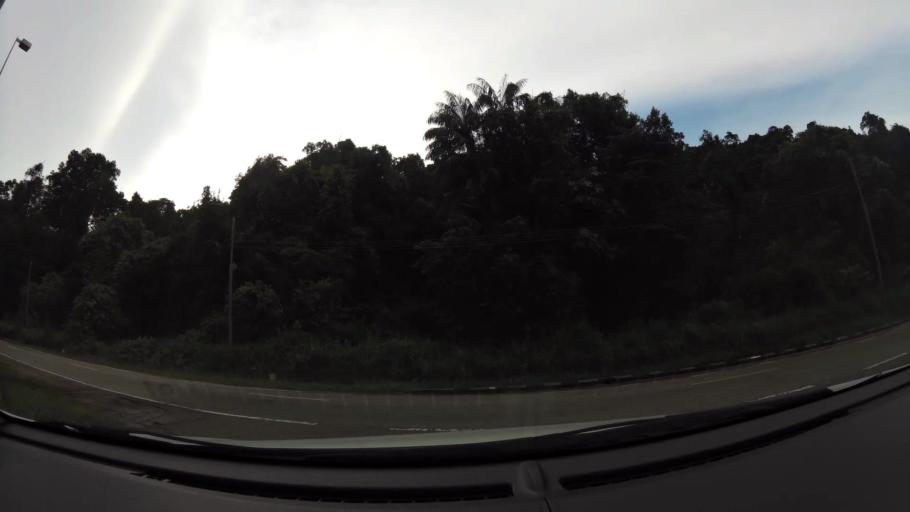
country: BN
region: Brunei and Muara
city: Bandar Seri Begawan
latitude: 4.9117
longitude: 115.0010
